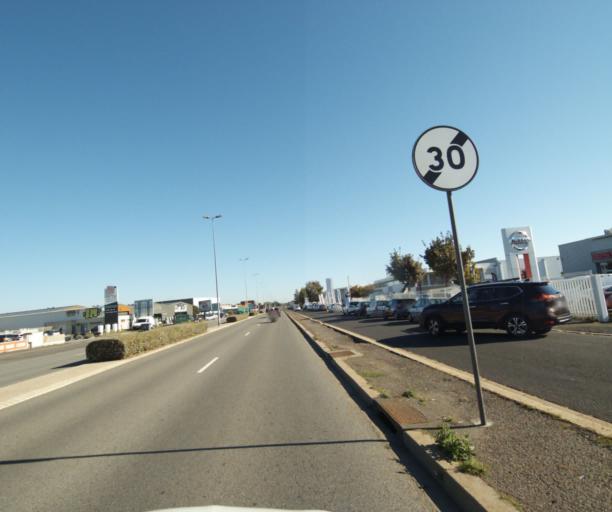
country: FR
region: Auvergne
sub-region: Departement du Puy-de-Dome
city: Aulnat
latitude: 45.7831
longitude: 3.1342
